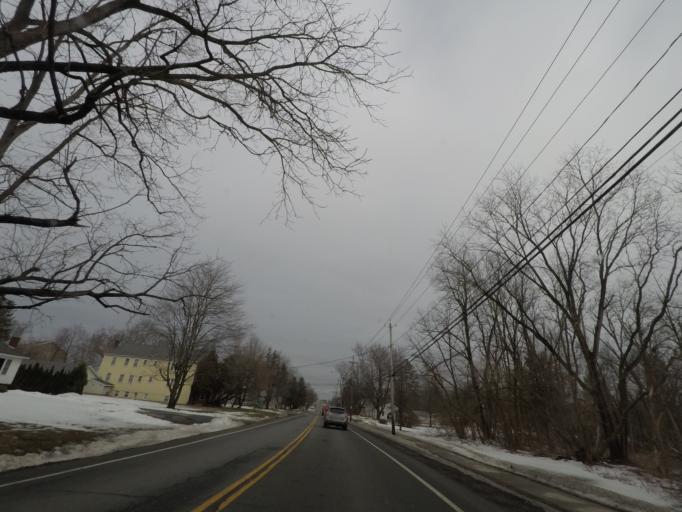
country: US
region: New York
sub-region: Albany County
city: Voorheesville
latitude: 42.7022
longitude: -73.9628
